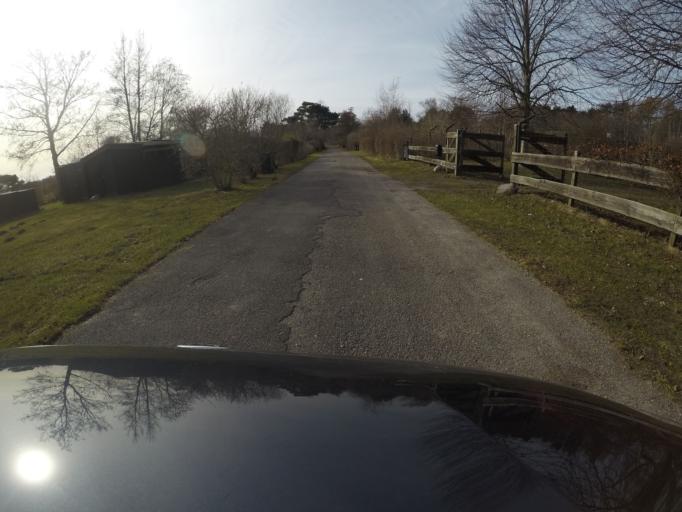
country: DK
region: Capital Region
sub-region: Halsnaes Kommune
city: Liseleje
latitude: 55.9937
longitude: 11.9226
